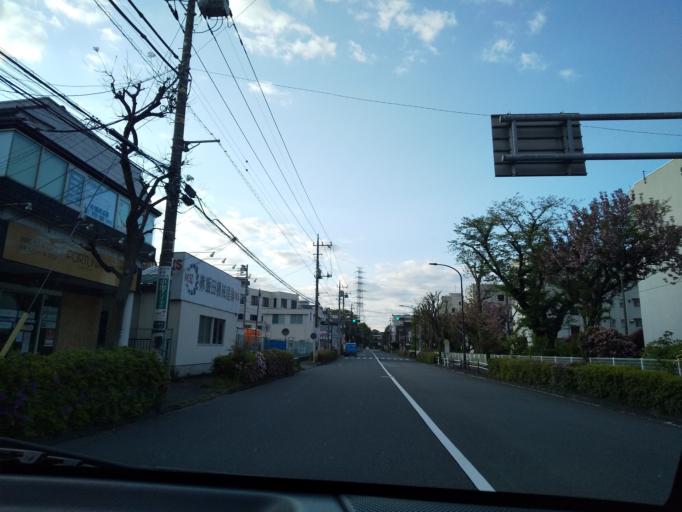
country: JP
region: Tokyo
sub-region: Machida-shi
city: Machida
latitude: 35.5577
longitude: 139.4254
